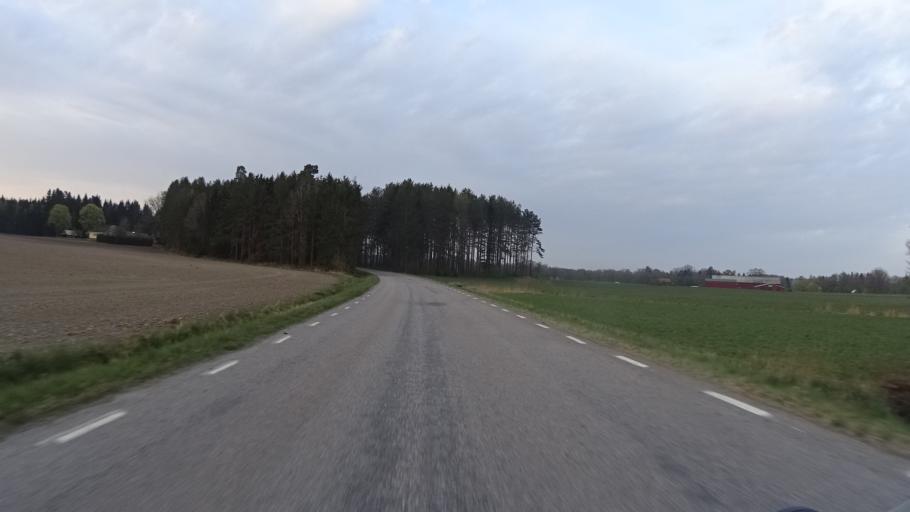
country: SE
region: Vaestra Goetaland
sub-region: Lidkopings Kommun
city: Vinninga
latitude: 58.4392
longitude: 13.3376
